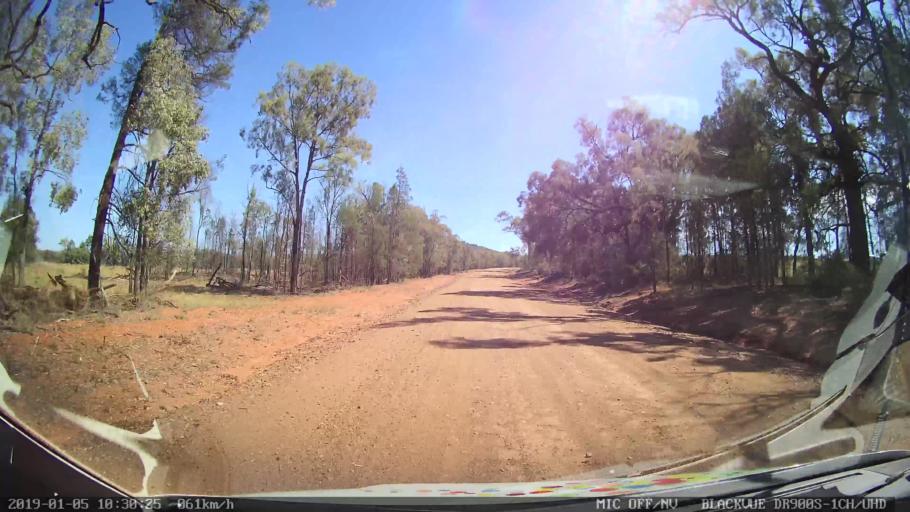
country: AU
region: New South Wales
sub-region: Gilgandra
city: Gilgandra
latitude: -31.5326
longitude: 148.9248
